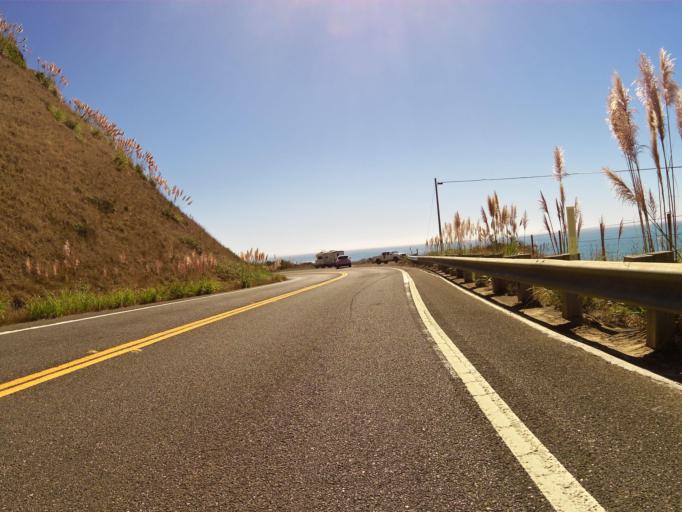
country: US
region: California
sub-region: Mendocino County
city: Fort Bragg
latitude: 39.6956
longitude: -123.7985
